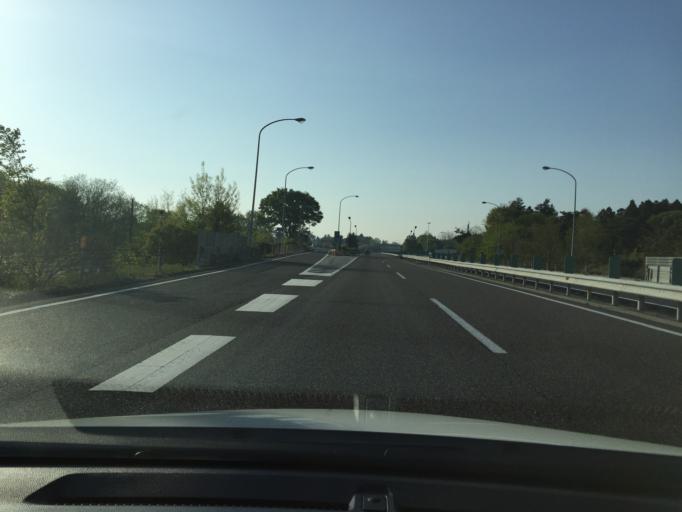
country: JP
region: Fukushima
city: Koriyama
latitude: 37.3554
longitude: 140.3201
